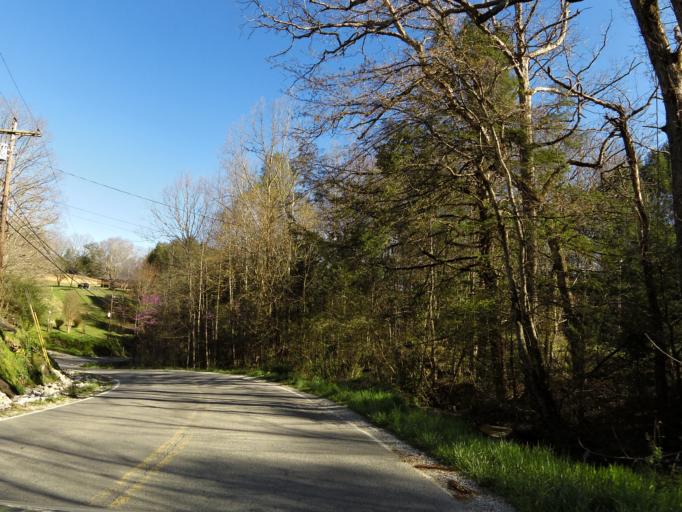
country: US
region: Tennessee
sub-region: Scott County
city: Huntsville
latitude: 36.3755
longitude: -84.3933
